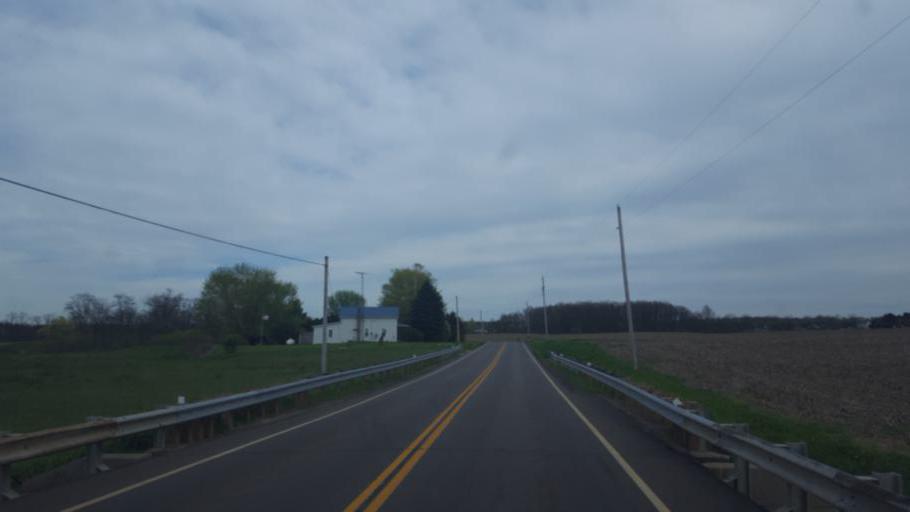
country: US
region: Ohio
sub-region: Crawford County
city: Galion
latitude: 40.7037
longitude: -82.7095
